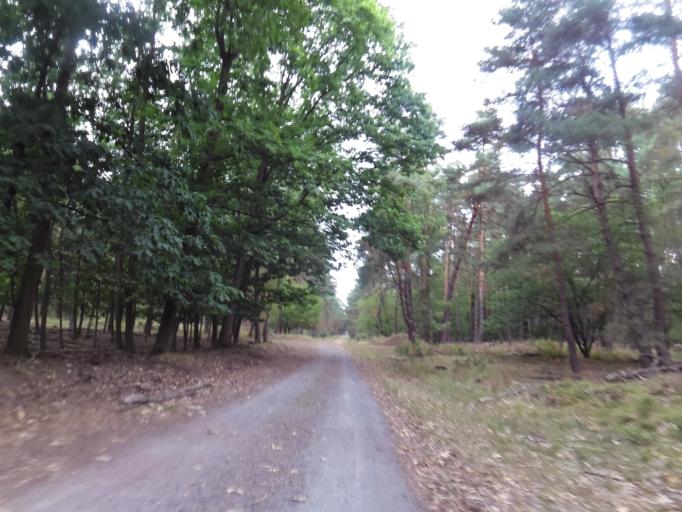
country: DE
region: Hesse
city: Morfelden-Walldorf
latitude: 50.0171
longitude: 8.5549
